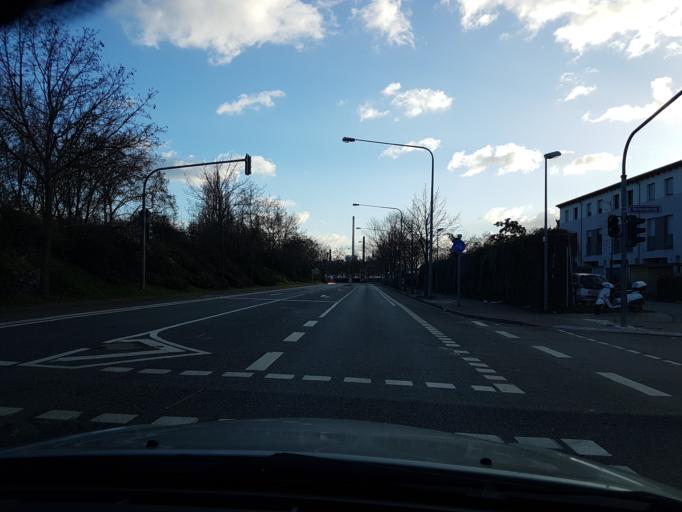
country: DE
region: Hesse
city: Sulzbach
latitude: 50.1045
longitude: 8.5287
